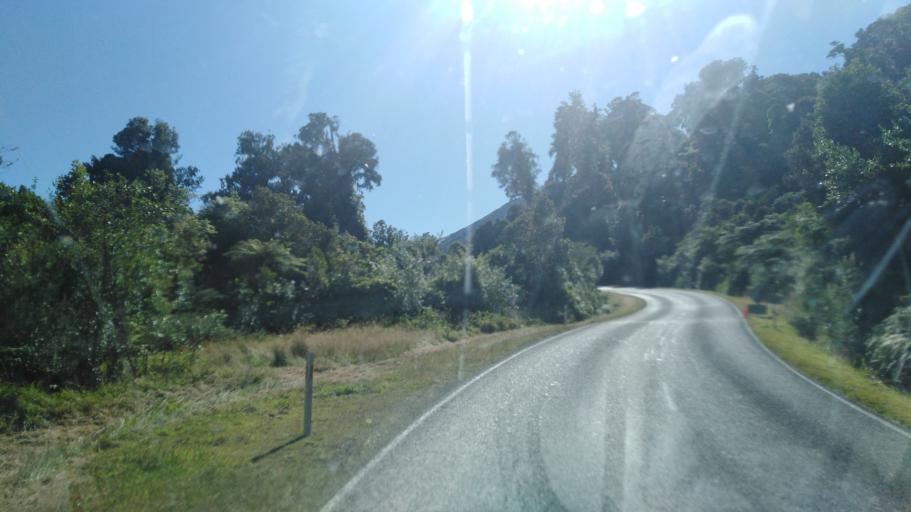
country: NZ
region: West Coast
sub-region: Buller District
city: Westport
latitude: -41.5298
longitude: 171.9941
